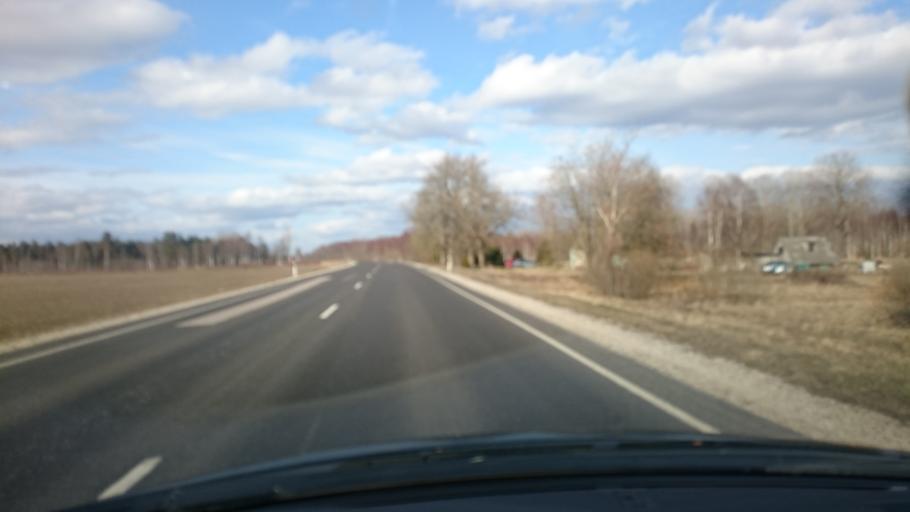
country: EE
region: Laeaene
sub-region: Lihula vald
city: Lihula
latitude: 58.8469
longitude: 24.0646
